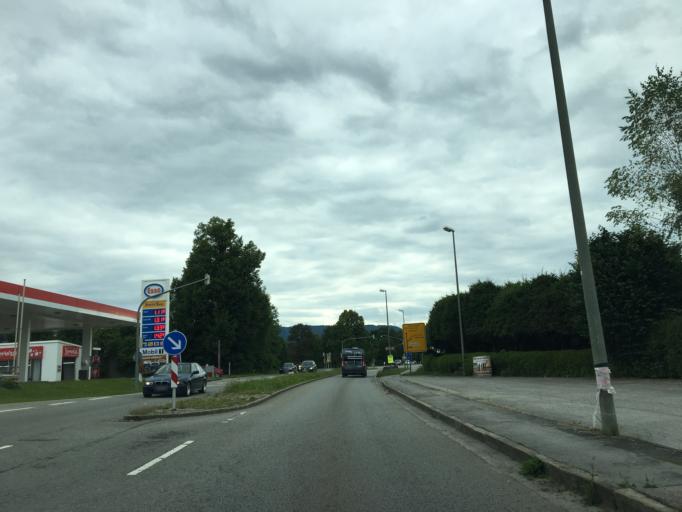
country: DE
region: Bavaria
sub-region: Upper Bavaria
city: Miesbach
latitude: 47.7833
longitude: 11.8345
